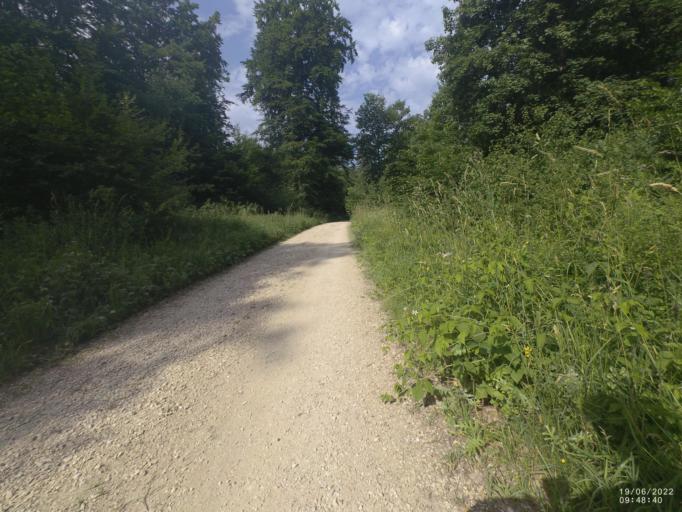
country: DE
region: Baden-Wuerttemberg
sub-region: Regierungsbezirk Stuttgart
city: Gerstetten
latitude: 48.6085
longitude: 10.0160
